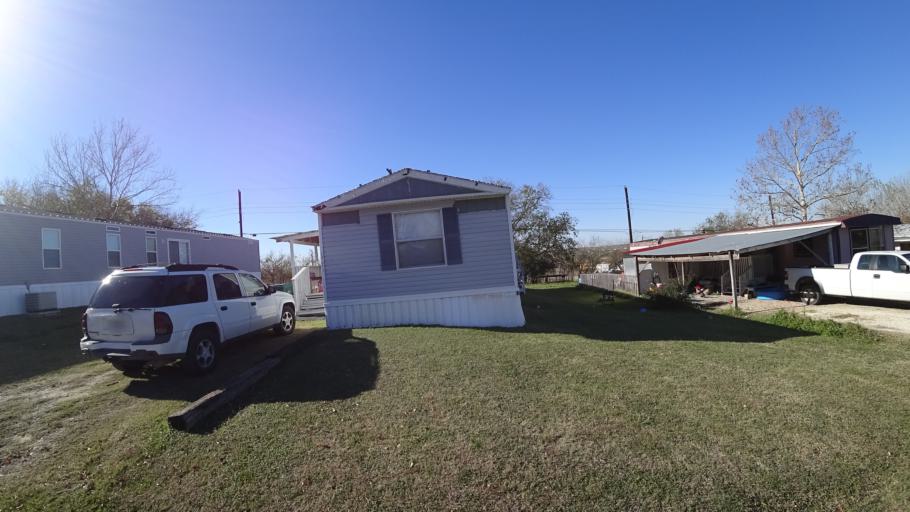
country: US
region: Texas
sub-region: Travis County
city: Onion Creek
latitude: 30.1062
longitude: -97.6726
